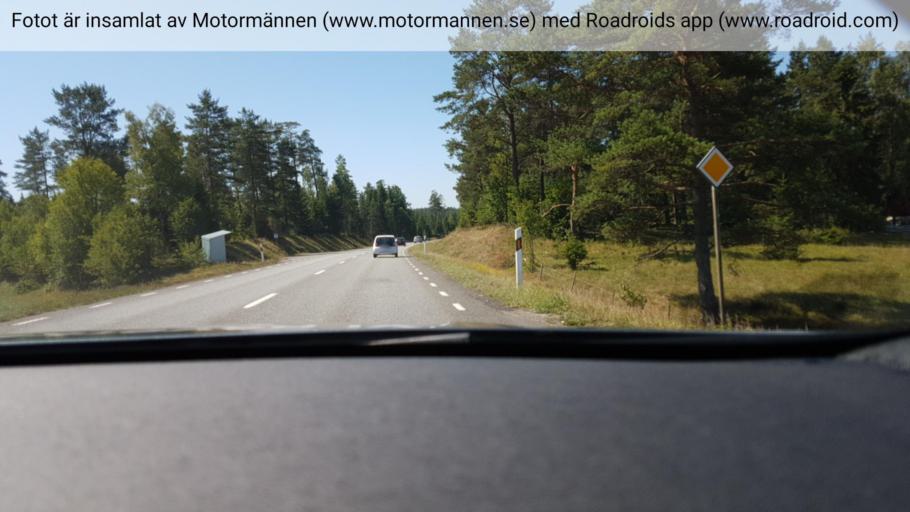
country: SE
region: Joenkoeping
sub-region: Gnosjo Kommun
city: Marieholm
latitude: 57.6461
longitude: 13.8065
